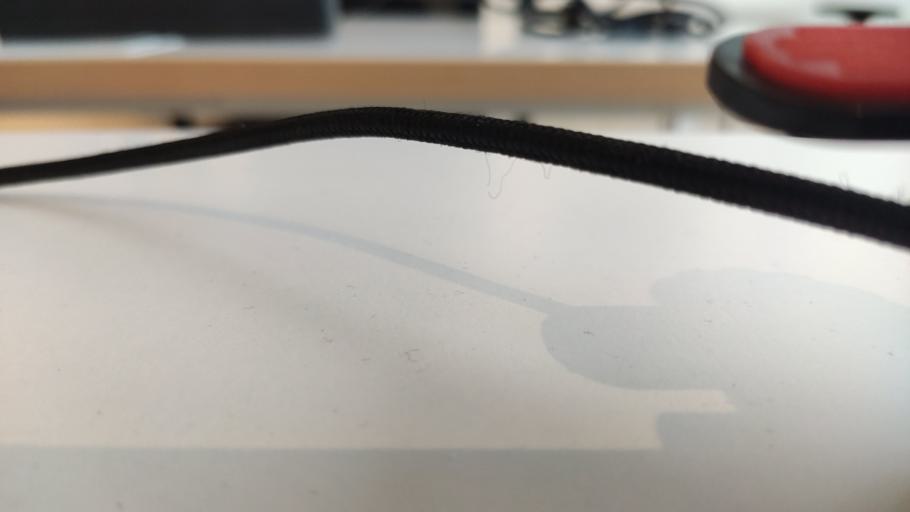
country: RU
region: Moskovskaya
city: Klin
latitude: 56.3529
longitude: 36.7490
